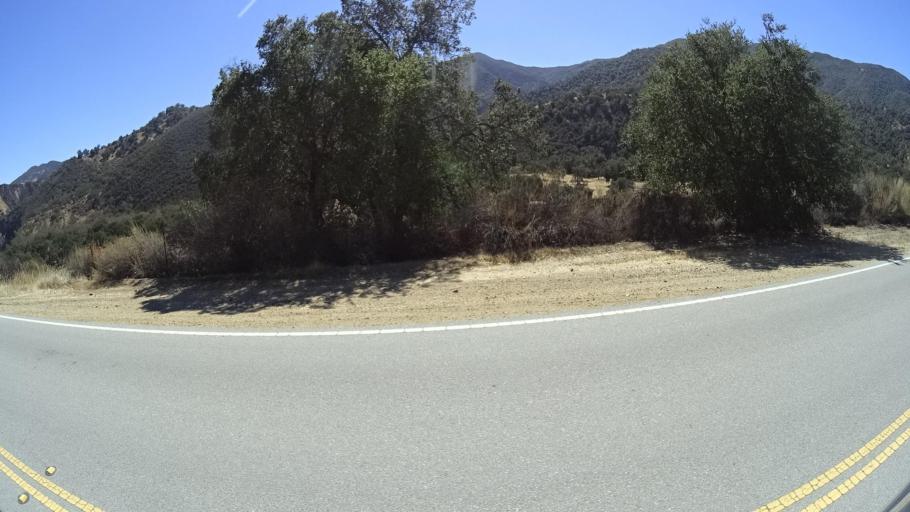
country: US
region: California
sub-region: Monterey County
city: Greenfield
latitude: 36.2342
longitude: -121.4560
